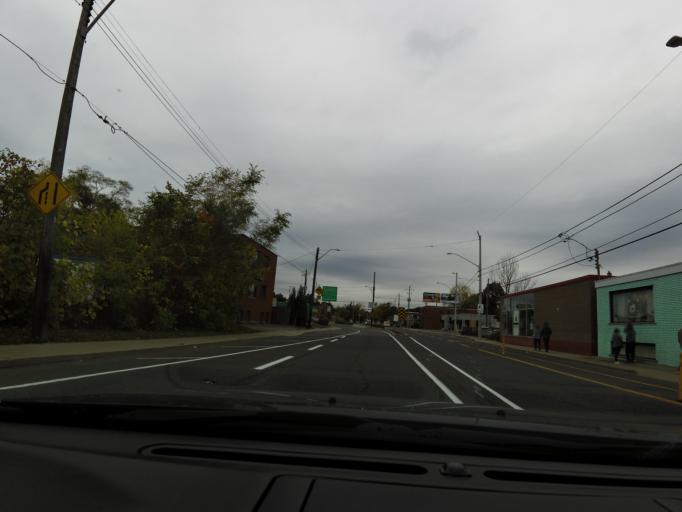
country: CA
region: Ontario
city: Hamilton
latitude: 43.2623
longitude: -79.8978
